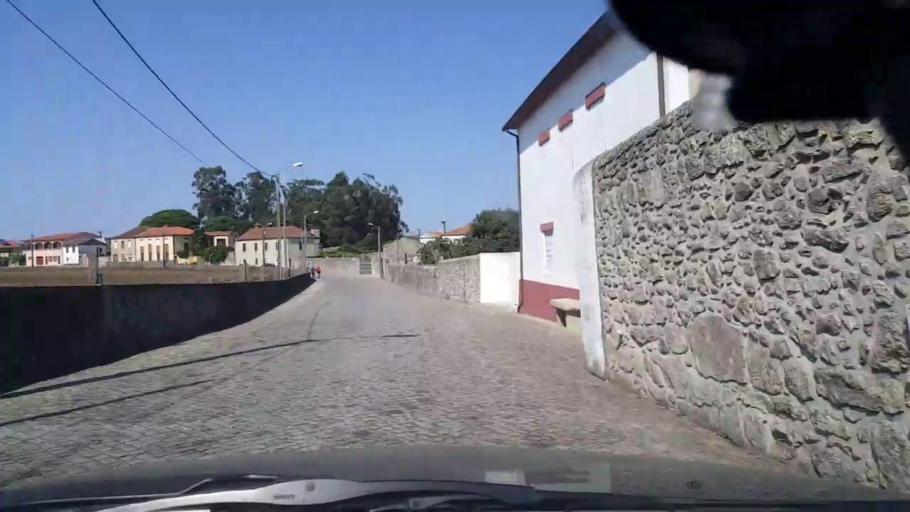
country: PT
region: Porto
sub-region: Vila do Conde
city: Arvore
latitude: 41.3833
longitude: -8.7034
